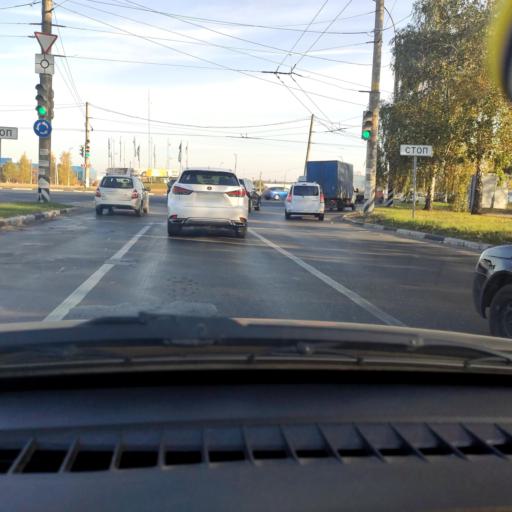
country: RU
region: Samara
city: Tol'yatti
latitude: 53.5512
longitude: 49.2669
